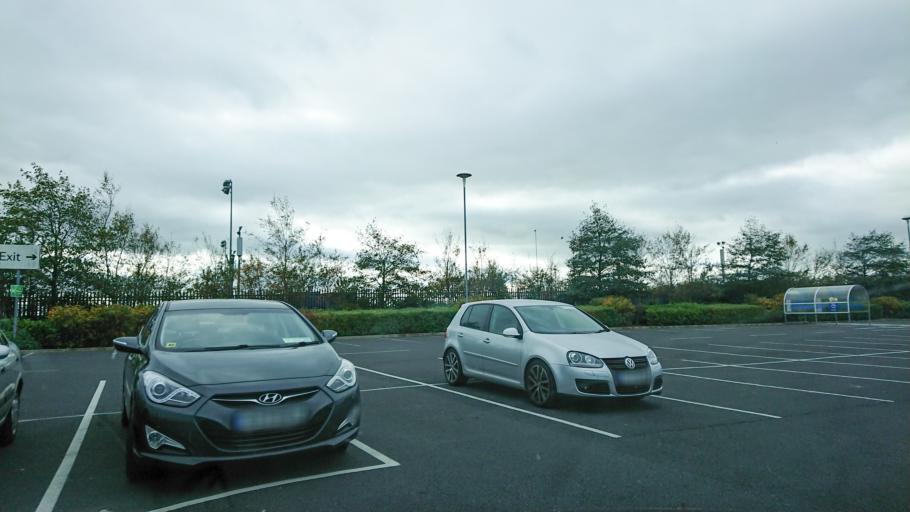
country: IE
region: Munster
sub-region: Waterford
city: Waterford
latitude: 52.2368
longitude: -7.1403
